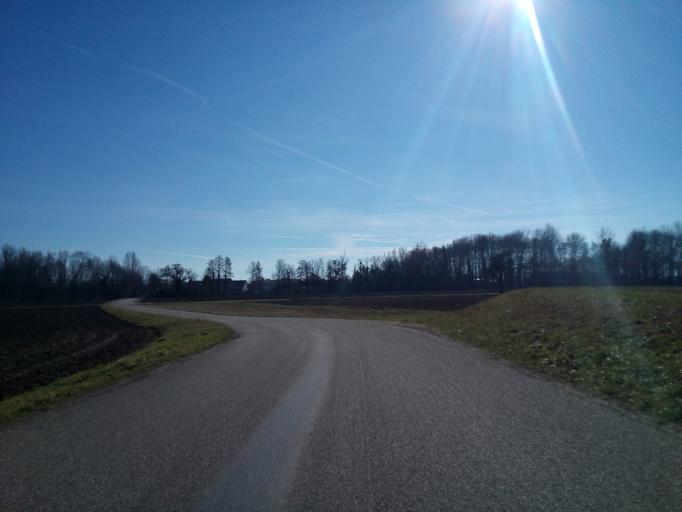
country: FR
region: Alsace
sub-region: Departement du Bas-Rhin
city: Gambsheim
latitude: 48.6535
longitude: 7.8865
